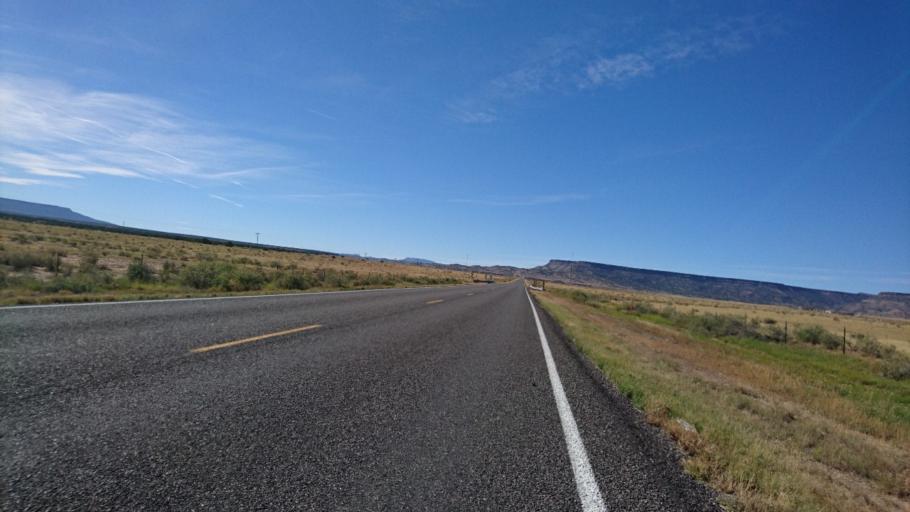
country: US
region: New Mexico
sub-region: Cibola County
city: Skyline-Ganipa
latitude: 35.0825
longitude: -107.6139
